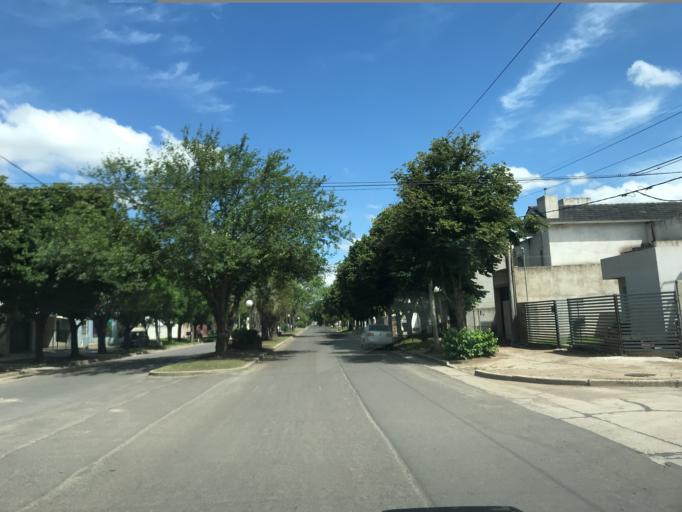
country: AR
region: Cordoba
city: Las Perdices
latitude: -32.7528
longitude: -63.7850
